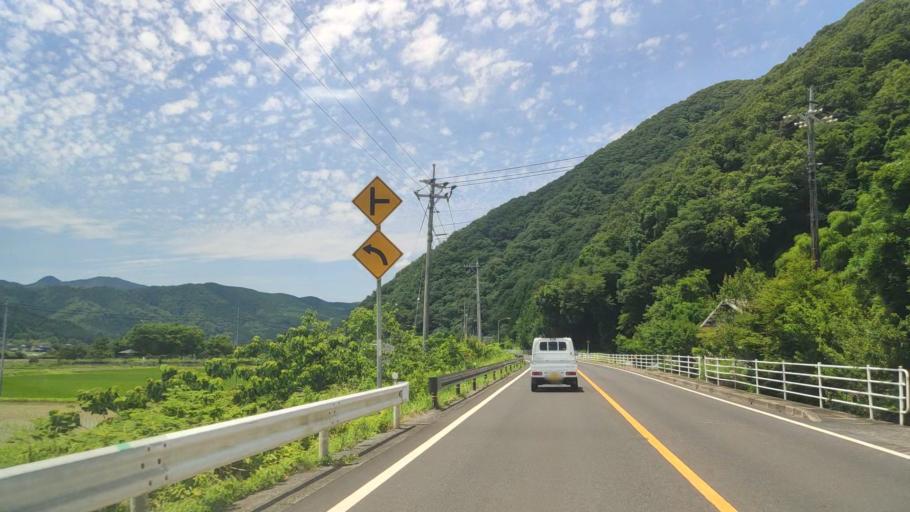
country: JP
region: Tottori
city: Tottori
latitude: 35.3671
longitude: 134.3325
